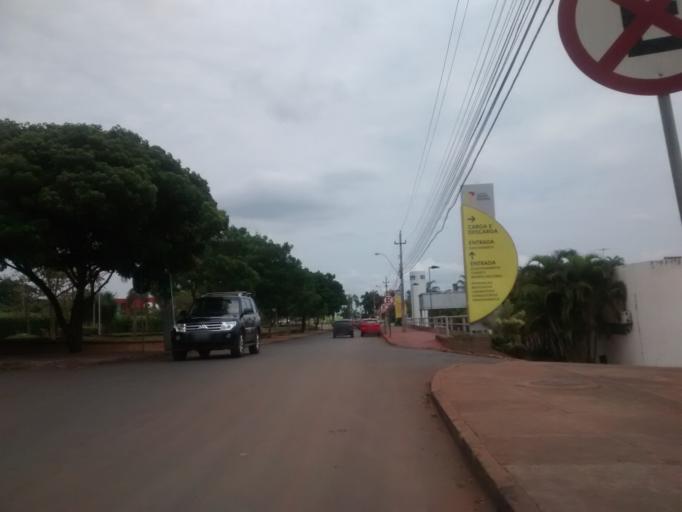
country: BR
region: Federal District
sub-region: Brasilia
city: Brasilia
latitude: -15.7366
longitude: -47.8968
